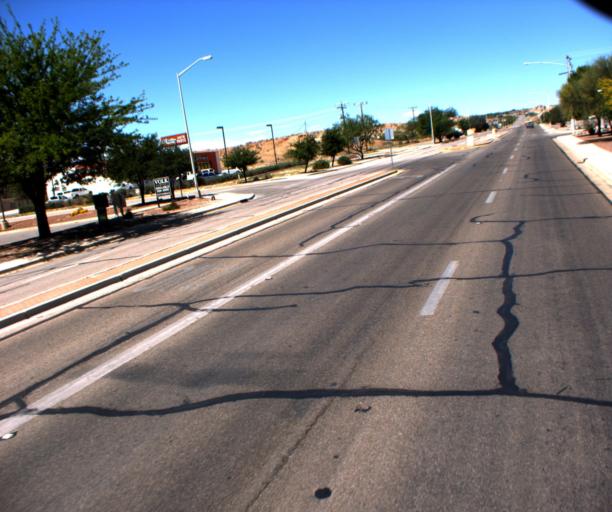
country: US
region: Arizona
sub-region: Cochise County
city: Benson
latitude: 31.9711
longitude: -110.3152
